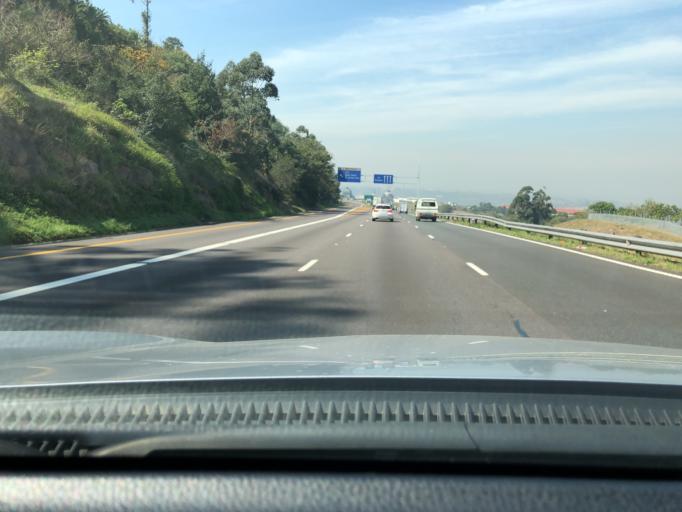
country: ZA
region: KwaZulu-Natal
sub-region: eThekwini Metropolitan Municipality
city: Berea
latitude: -29.8457
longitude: 30.9249
